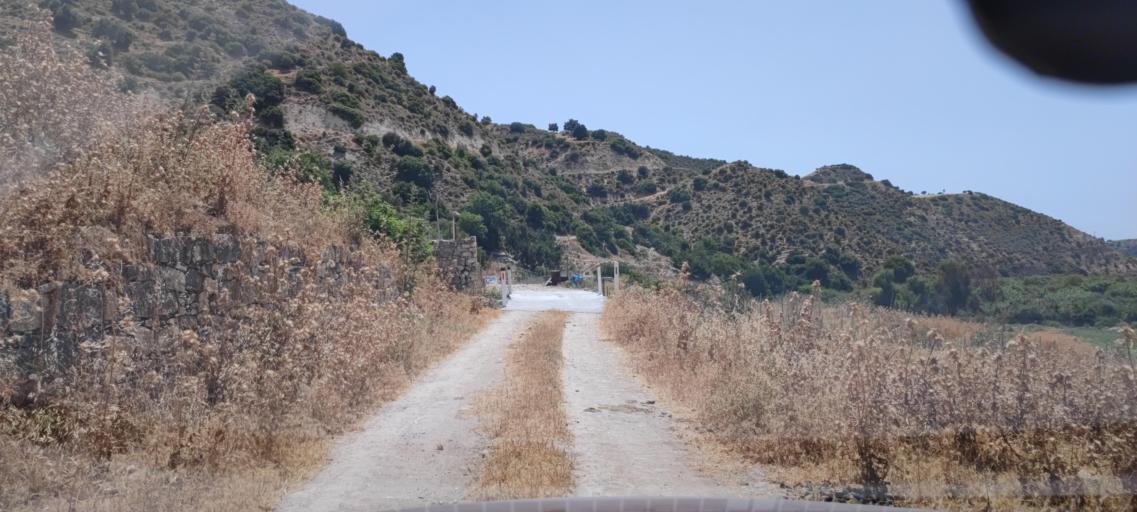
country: CY
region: Limassol
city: Pissouri
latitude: 34.7321
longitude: 32.6008
